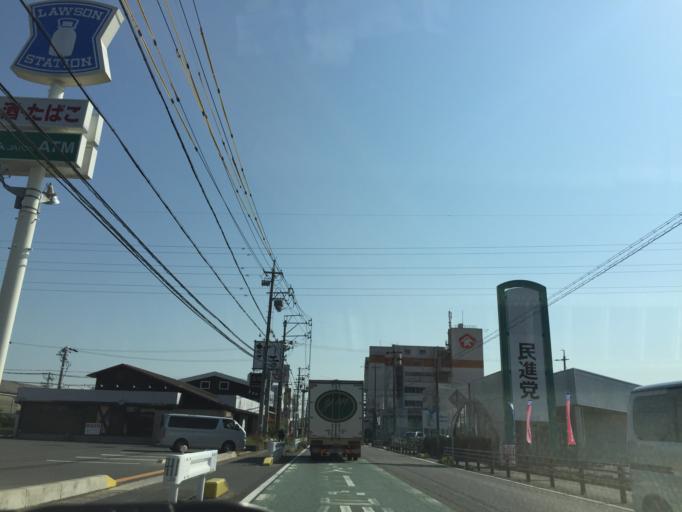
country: JP
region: Mie
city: Yokkaichi
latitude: 35.0176
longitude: 136.6648
